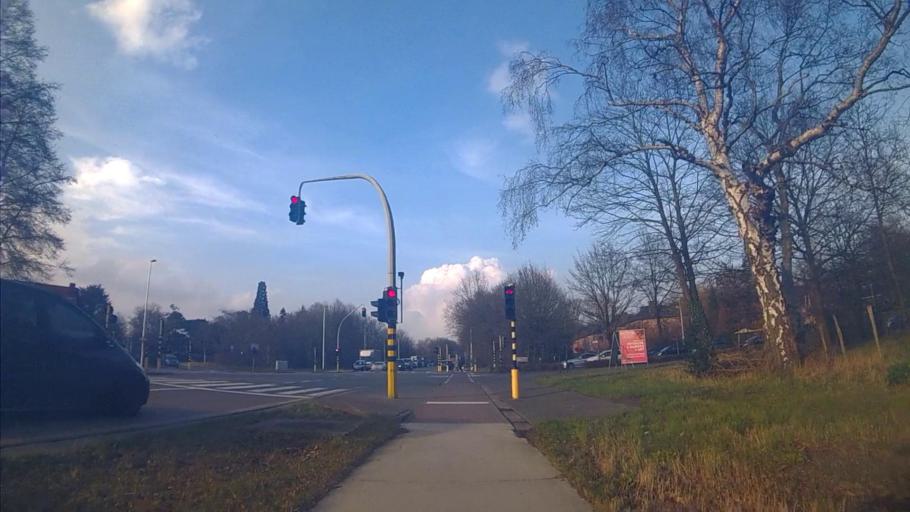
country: BE
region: Flanders
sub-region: Provincie Oost-Vlaanderen
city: Destelbergen
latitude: 51.0659
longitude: 3.7662
